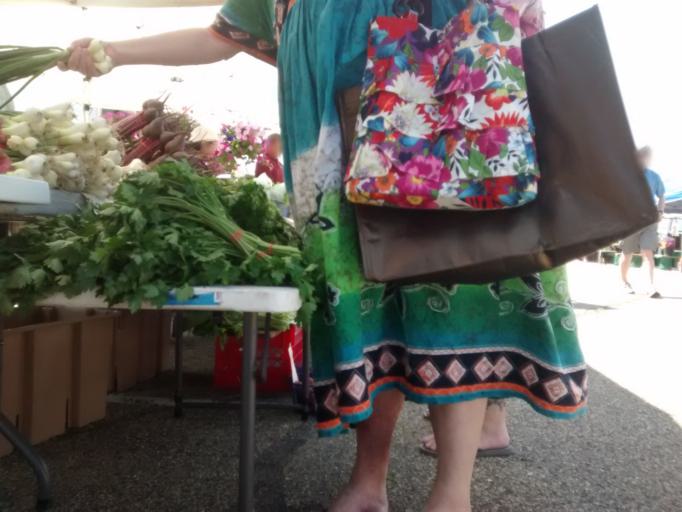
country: US
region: Minnesota
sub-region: Dakota County
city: Burnsville
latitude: 44.7720
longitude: -93.2814
